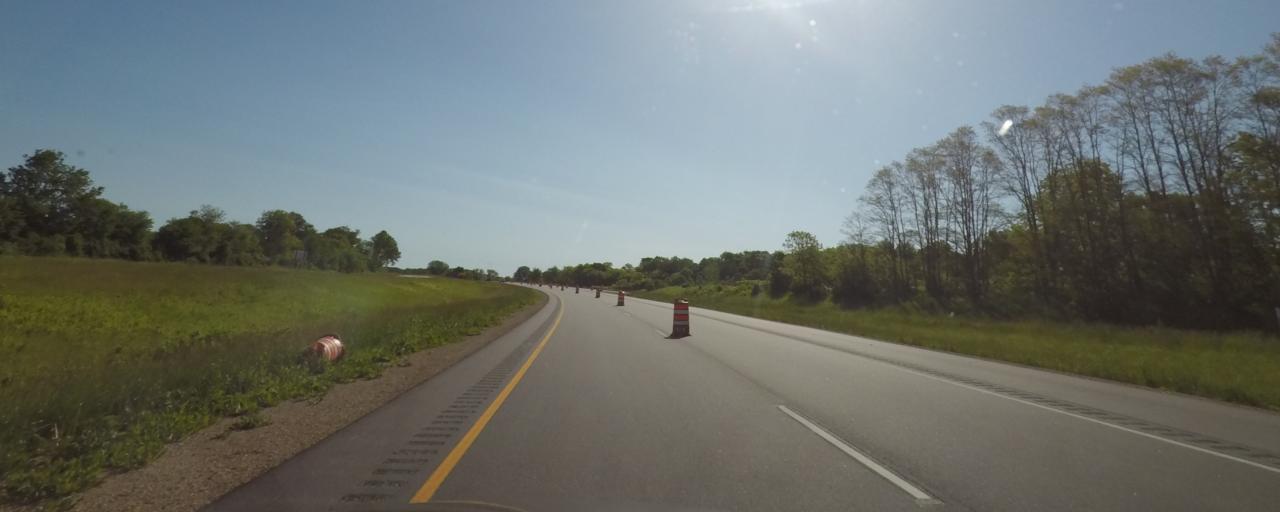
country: US
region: Wisconsin
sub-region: Columbia County
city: Columbus
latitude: 43.3581
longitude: -88.9919
